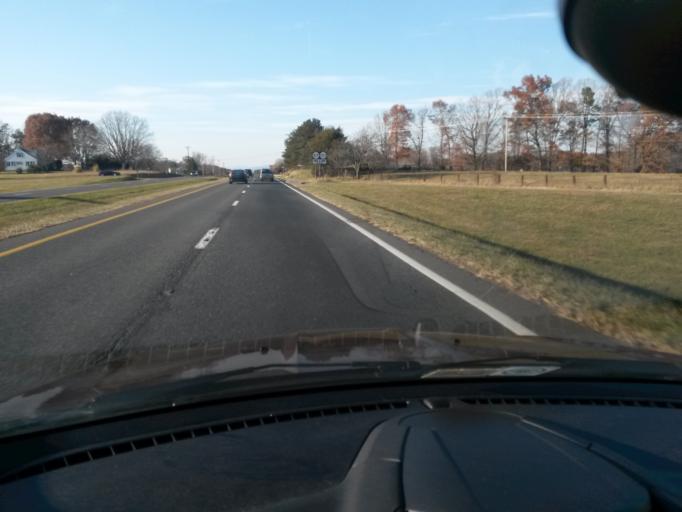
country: US
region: Virginia
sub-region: Campbell County
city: Concord
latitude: 37.3619
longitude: -79.0065
